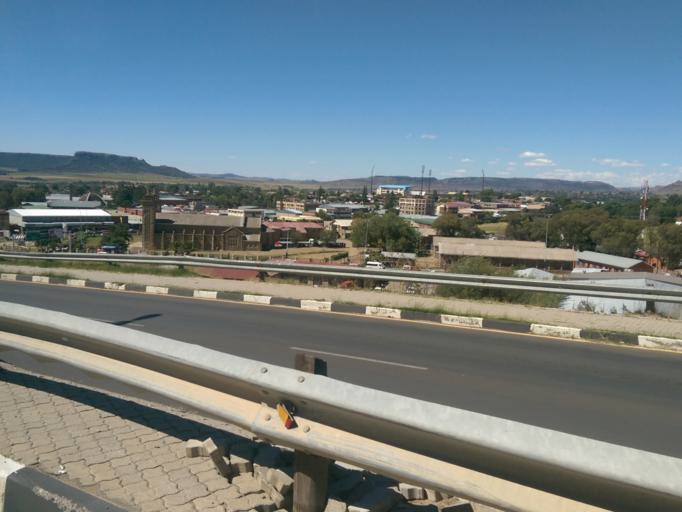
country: LS
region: Maseru
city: Maseru
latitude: -29.3192
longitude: 27.4940
